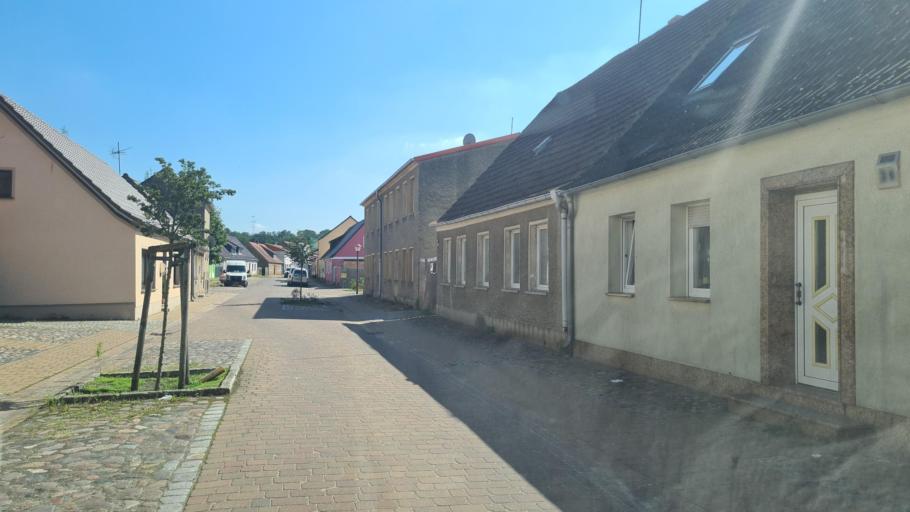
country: DE
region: Brandenburg
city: Friesack
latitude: 52.7398
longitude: 12.5845
